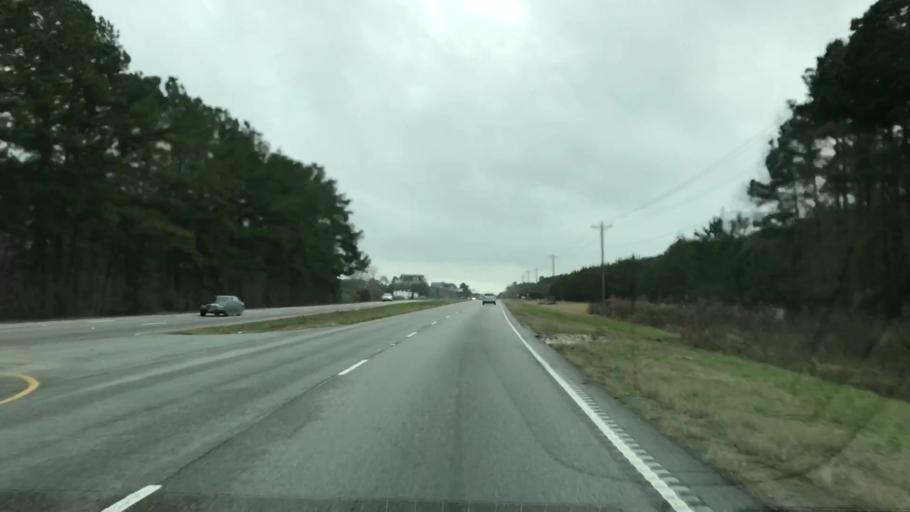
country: US
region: South Carolina
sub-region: Berkeley County
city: Goose Creek
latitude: 33.0424
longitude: -80.0333
